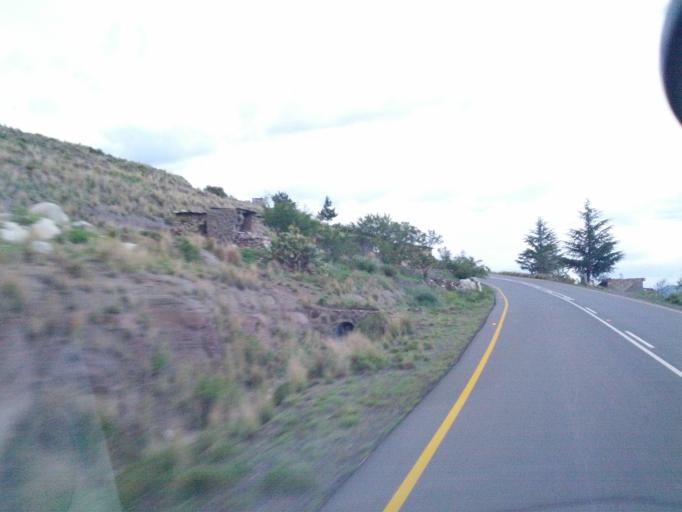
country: LS
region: Qacha's Nek
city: Qacha's Nek
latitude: -30.0294
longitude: 28.3087
